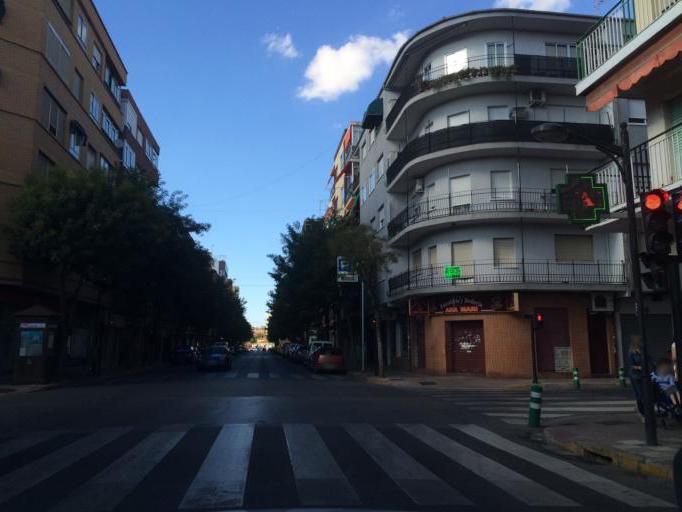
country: ES
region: Castille-La Mancha
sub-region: Provincia de Albacete
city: Albacete
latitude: 38.9940
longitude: -1.8671
